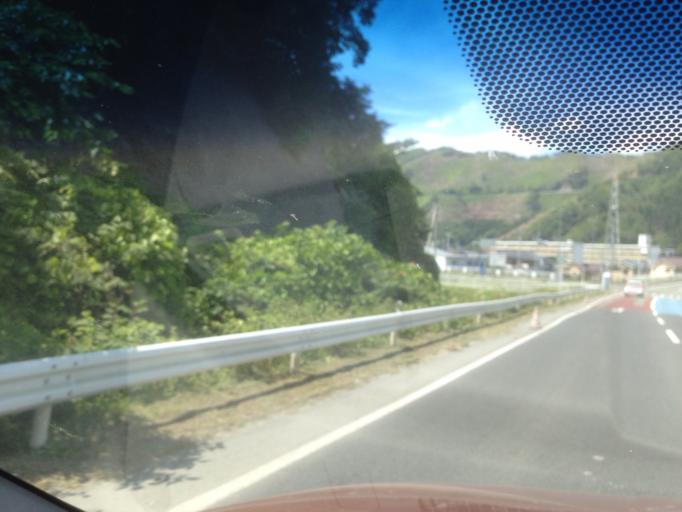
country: JP
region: Iwate
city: Otsuchi
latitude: 39.3535
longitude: 141.8930
